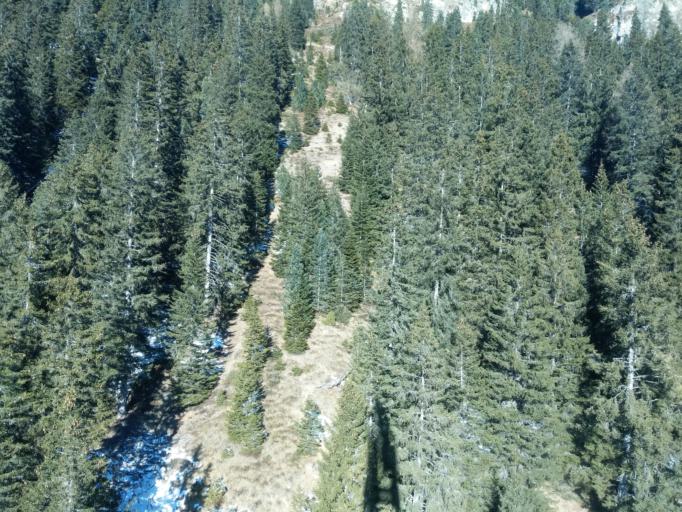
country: IT
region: Trentino-Alto Adige
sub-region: Provincia di Trento
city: Vigo di Fassa
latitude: 46.4306
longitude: 11.6668
